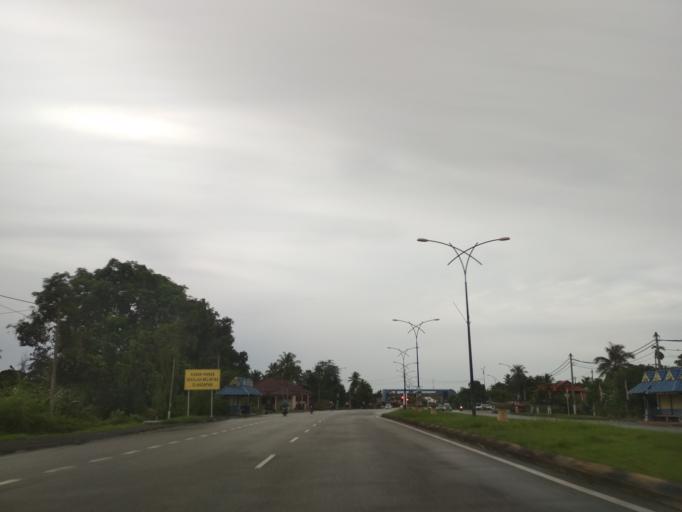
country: MY
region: Perlis
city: Kangar
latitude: 6.4634
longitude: 100.2090
